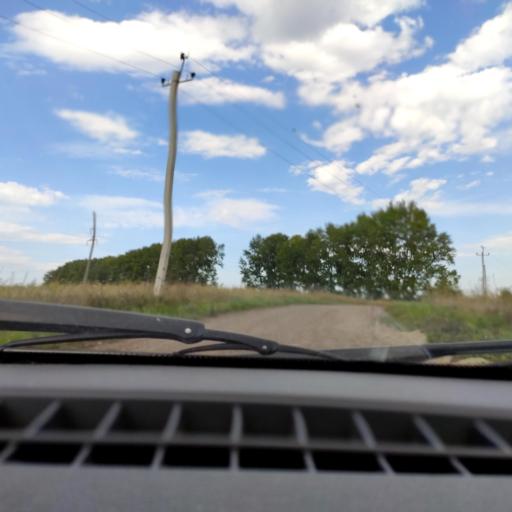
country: RU
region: Bashkortostan
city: Avdon
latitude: 54.7046
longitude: 55.7806
